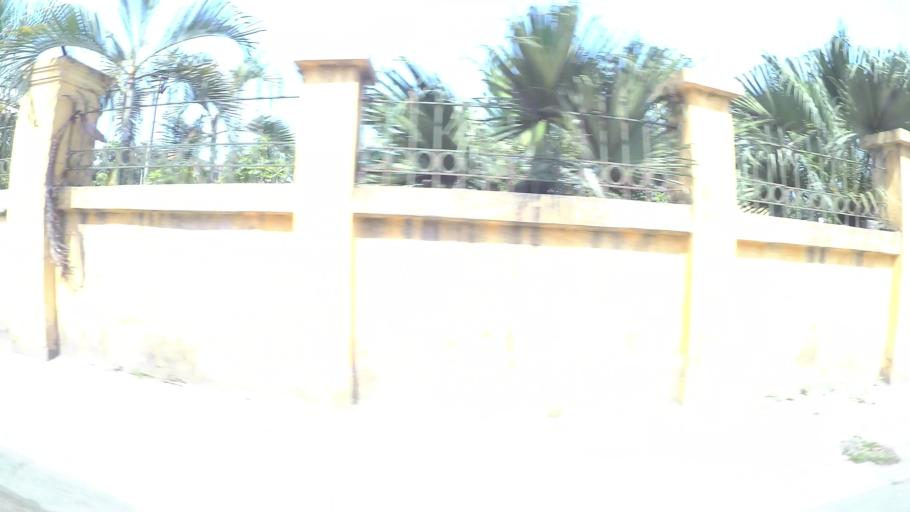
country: VN
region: Ha Noi
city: Hoan Kiem
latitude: 21.0557
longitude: 105.8771
